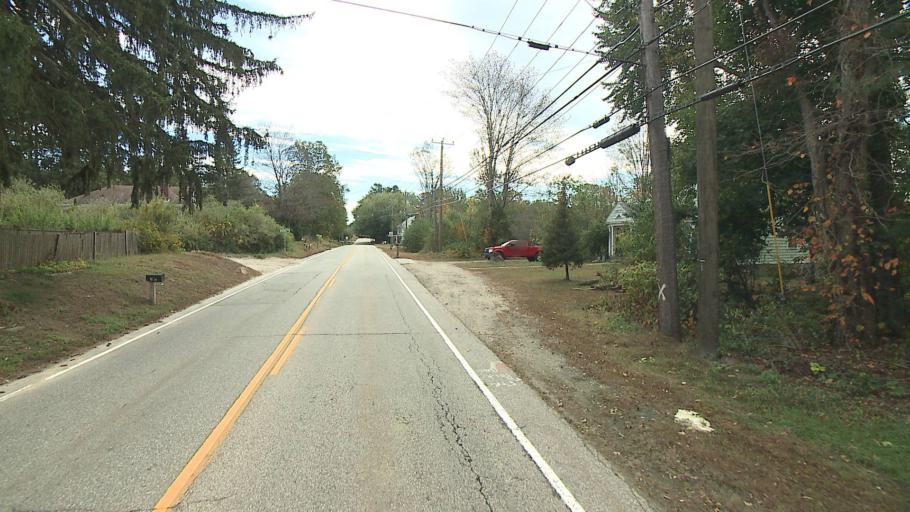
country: US
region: Connecticut
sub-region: Windham County
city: Killingly Center
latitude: 41.8608
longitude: -71.8822
